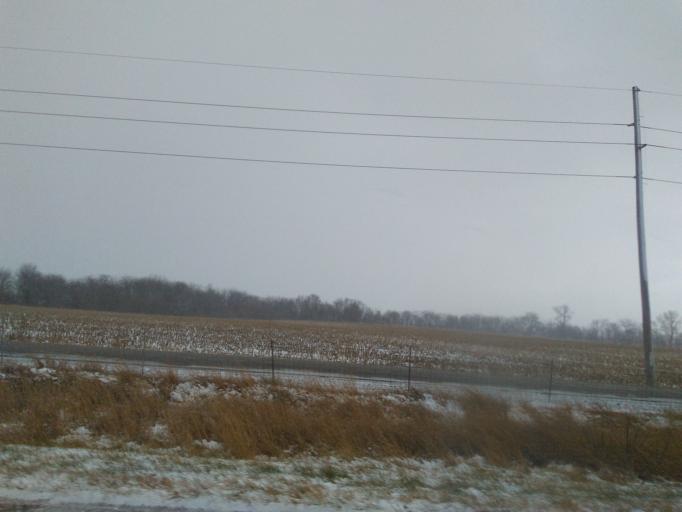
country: US
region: Illinois
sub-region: Madison County
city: Highland
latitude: 38.8078
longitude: -89.5842
